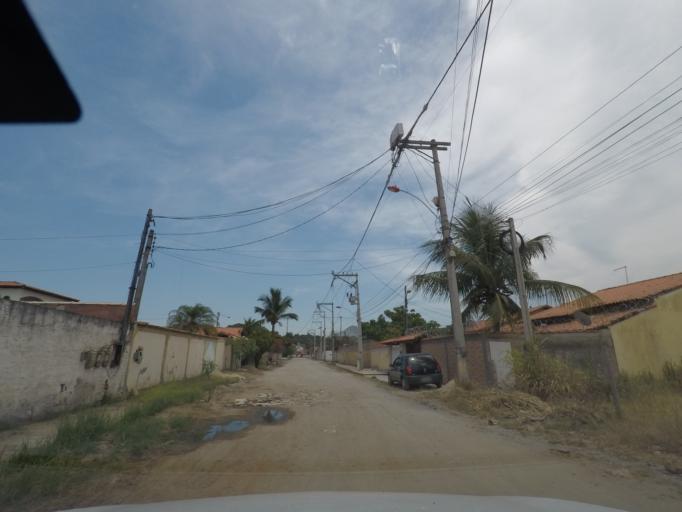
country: BR
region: Rio de Janeiro
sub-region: Niteroi
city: Niteroi
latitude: -22.9621
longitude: -42.9740
